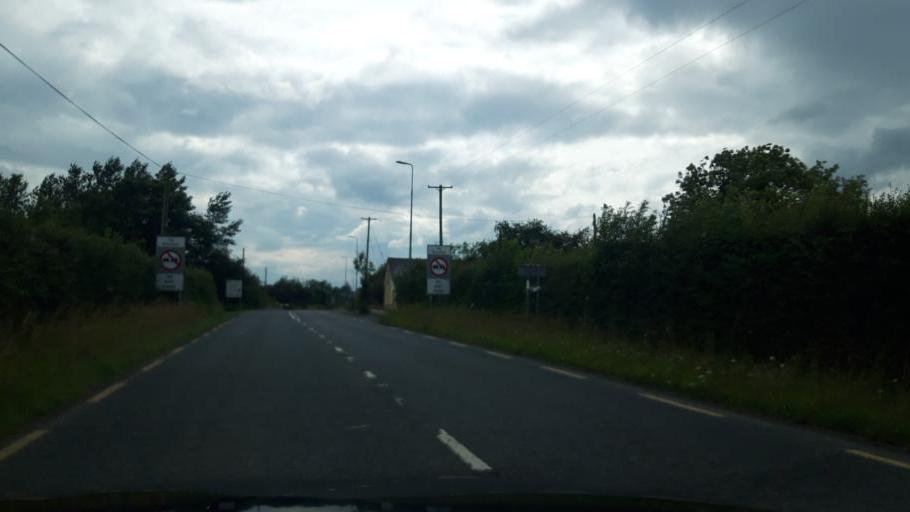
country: IE
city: Ballylinan
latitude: 52.8662
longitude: -7.1029
